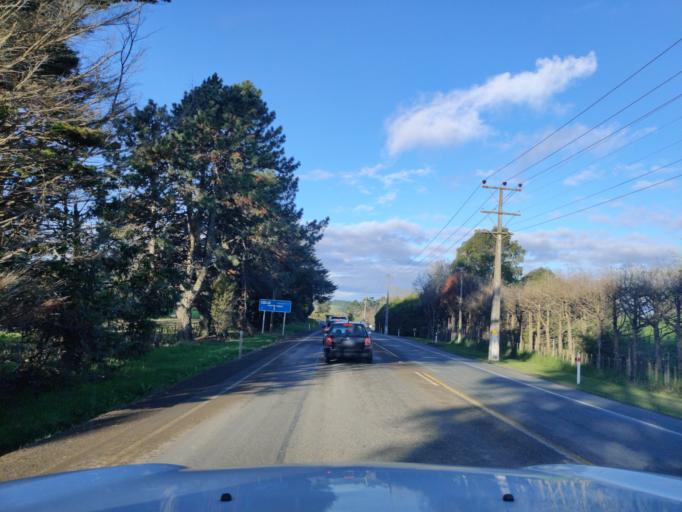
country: NZ
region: Auckland
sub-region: Auckland
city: Red Hill
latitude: -36.9736
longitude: 174.9900
